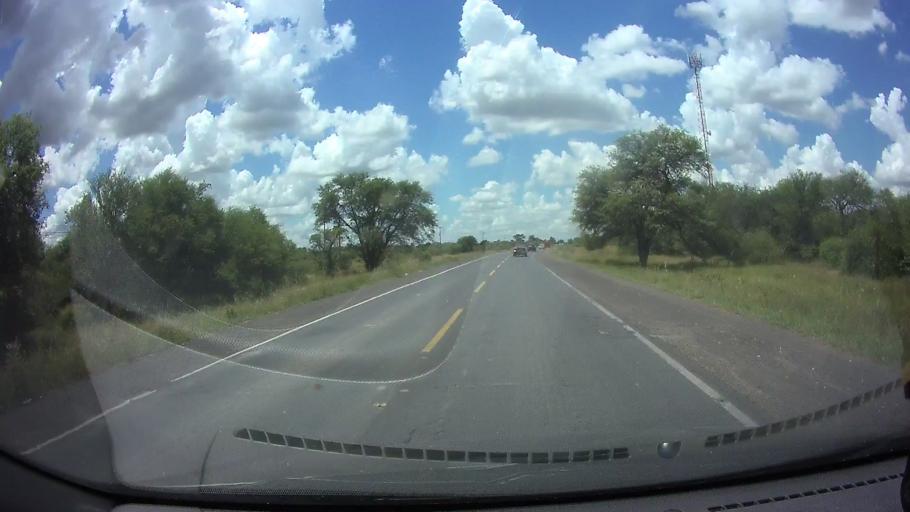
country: PY
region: Presidente Hayes
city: Nanawa
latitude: -25.2247
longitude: -57.6841
